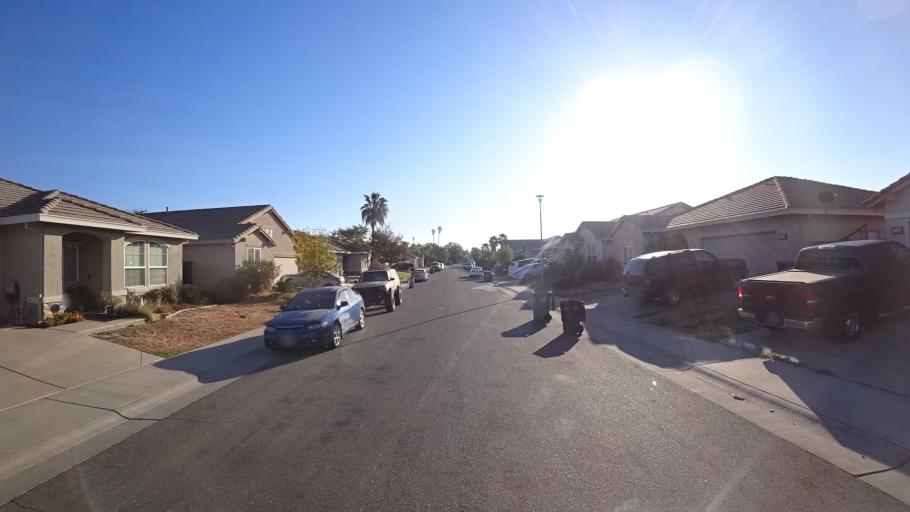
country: US
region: California
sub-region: Sacramento County
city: Parkway
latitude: 38.4774
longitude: -121.4940
